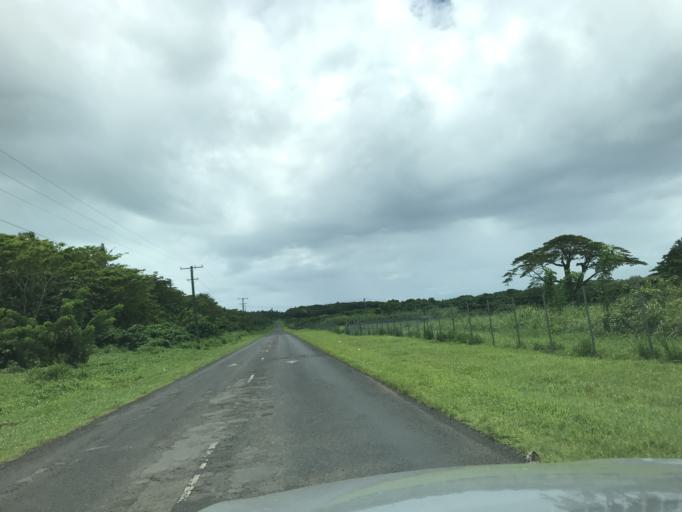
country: WS
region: A'ana
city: Satapuala
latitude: -13.8338
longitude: -172.0051
